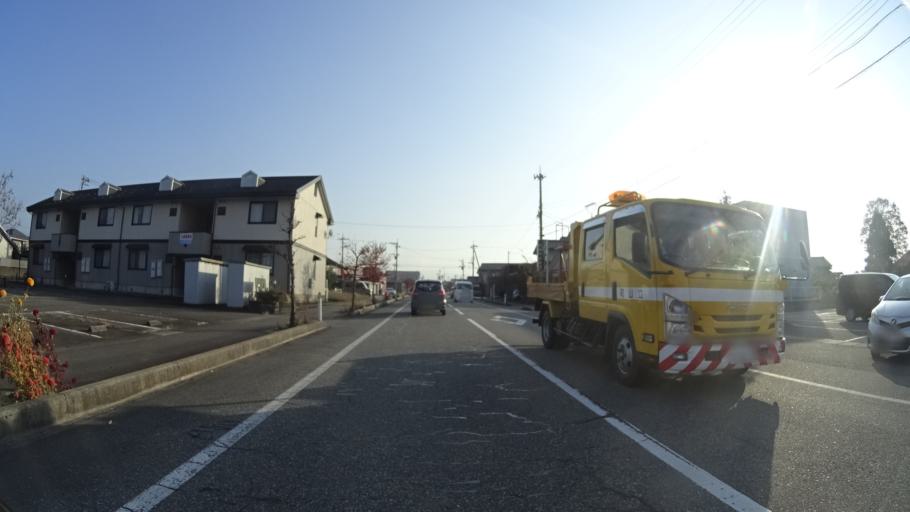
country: JP
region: Toyama
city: Kamiichi
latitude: 36.6599
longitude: 137.3125
